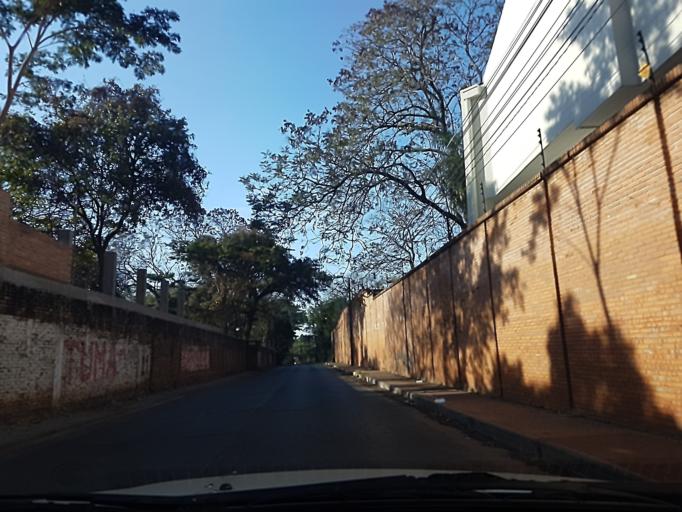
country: PY
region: Central
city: Fernando de la Mora
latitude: -25.2618
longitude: -57.5594
